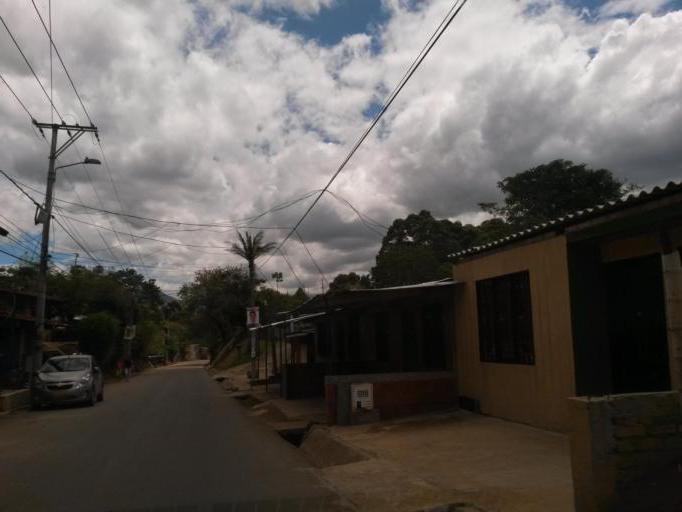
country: CO
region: Cauca
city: Popayan
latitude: 2.4795
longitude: -76.5677
